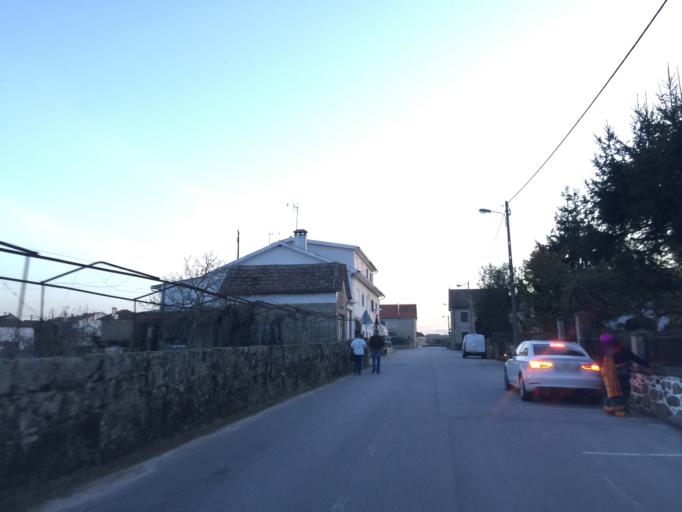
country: PT
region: Viseu
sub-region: Concelho de Carregal do Sal
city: Carregal do Sal
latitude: 40.4698
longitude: -7.9721
